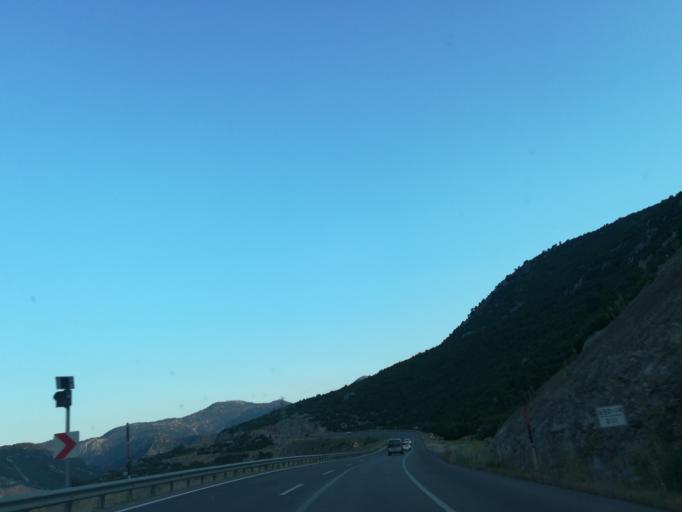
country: TR
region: Antalya
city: Dagbeli
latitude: 37.1673
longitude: 30.4987
